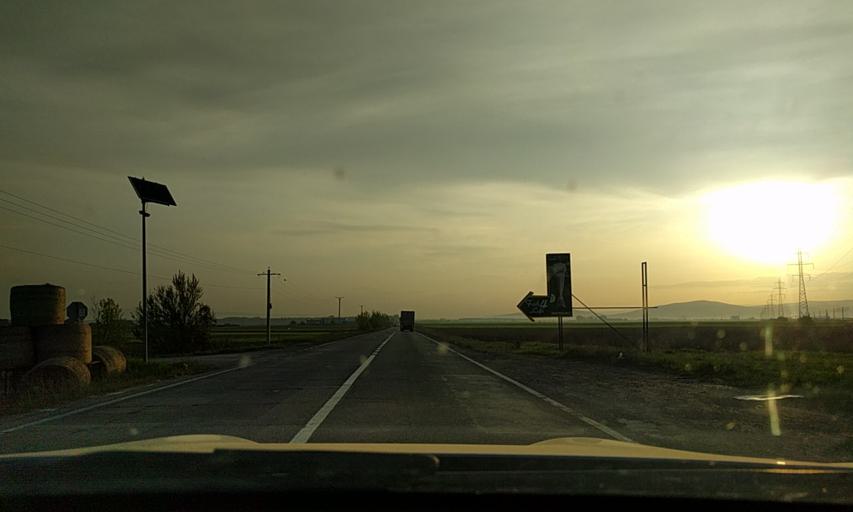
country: RO
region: Brasov
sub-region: Comuna Harman
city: Harman
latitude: 45.7149
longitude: 25.7130
